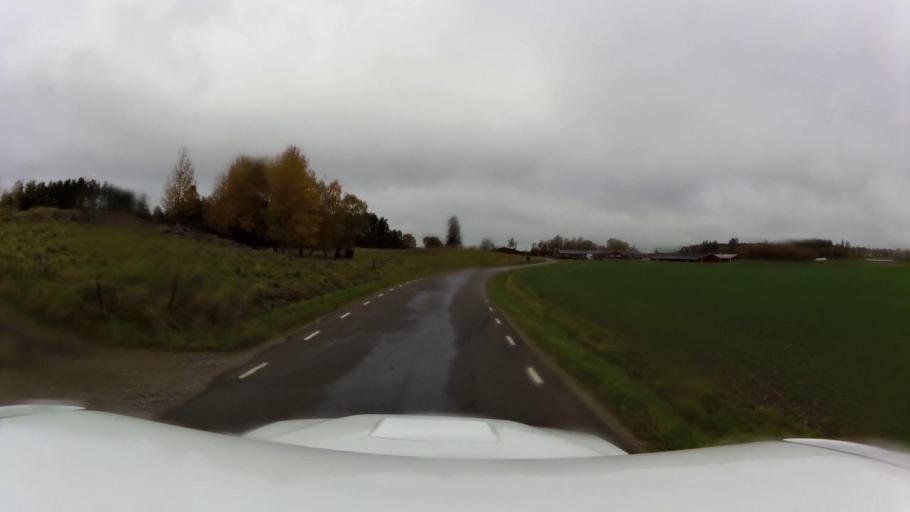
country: SE
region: OEstergoetland
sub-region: Linkopings Kommun
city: Linghem
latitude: 58.4746
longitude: 15.8186
